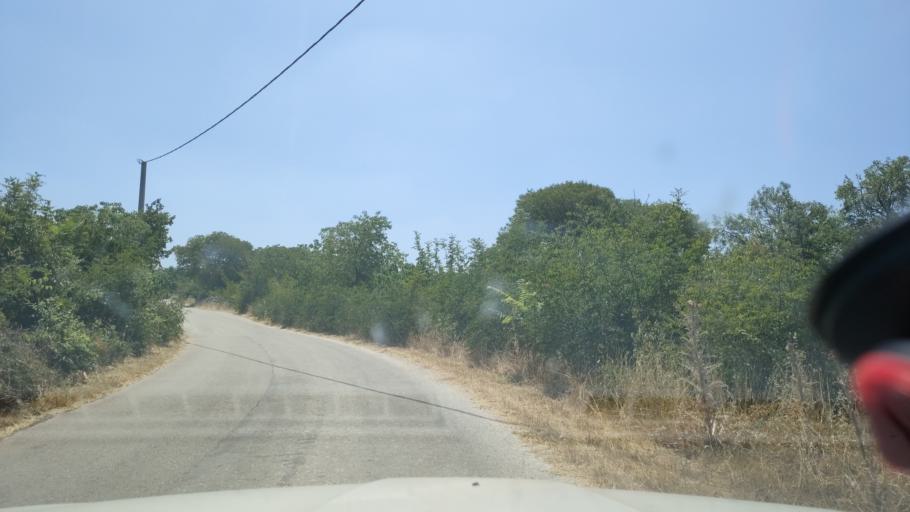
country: HR
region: Sibensko-Kniniska
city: Kistanje
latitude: 43.9517
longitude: 15.8820
